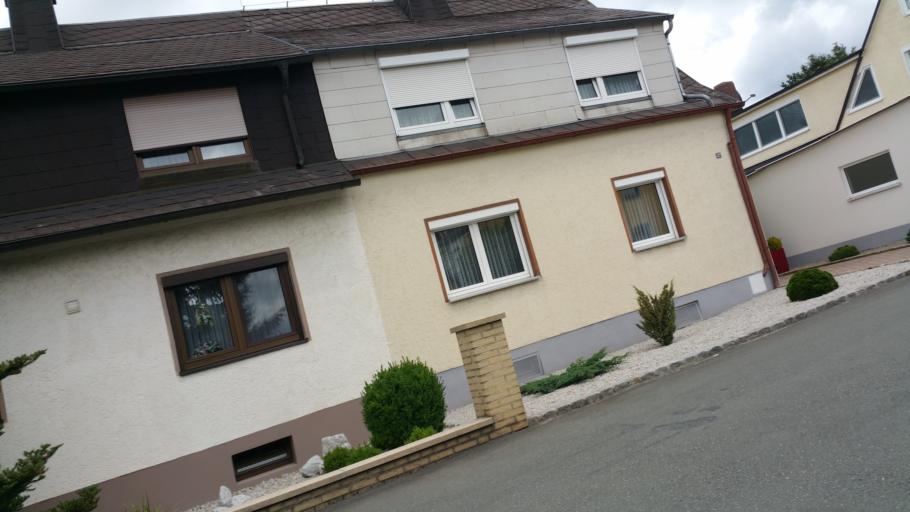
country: DE
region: Bavaria
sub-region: Upper Franconia
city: Rehau
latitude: 50.2376
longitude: 12.0217
